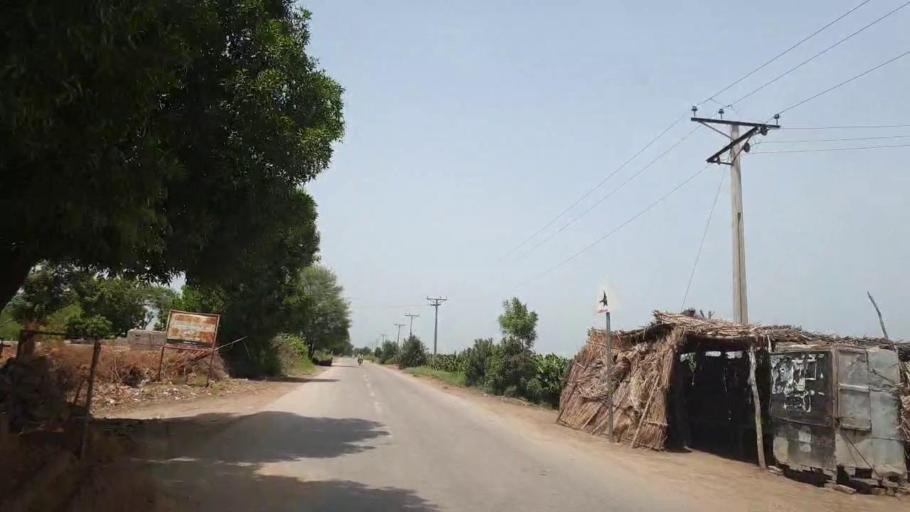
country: PK
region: Sindh
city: Sakrand
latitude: 26.1769
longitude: 68.2269
